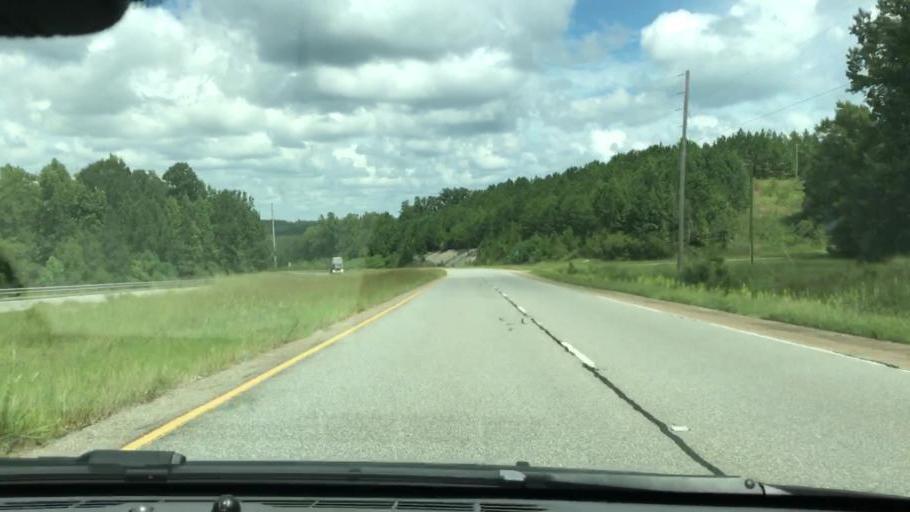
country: US
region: Georgia
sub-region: Stewart County
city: Lumpkin
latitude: 32.0948
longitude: -84.8097
